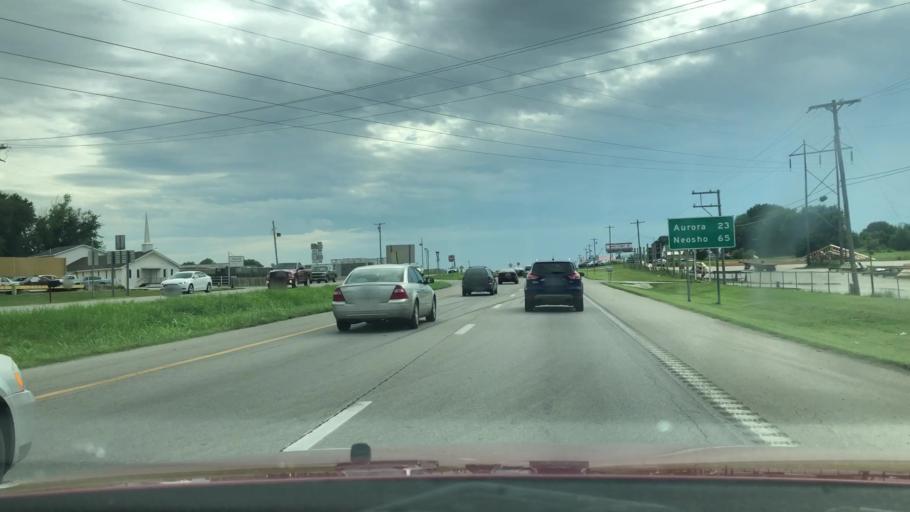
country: US
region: Missouri
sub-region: Greene County
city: Battlefield
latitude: 37.1604
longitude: -93.4014
